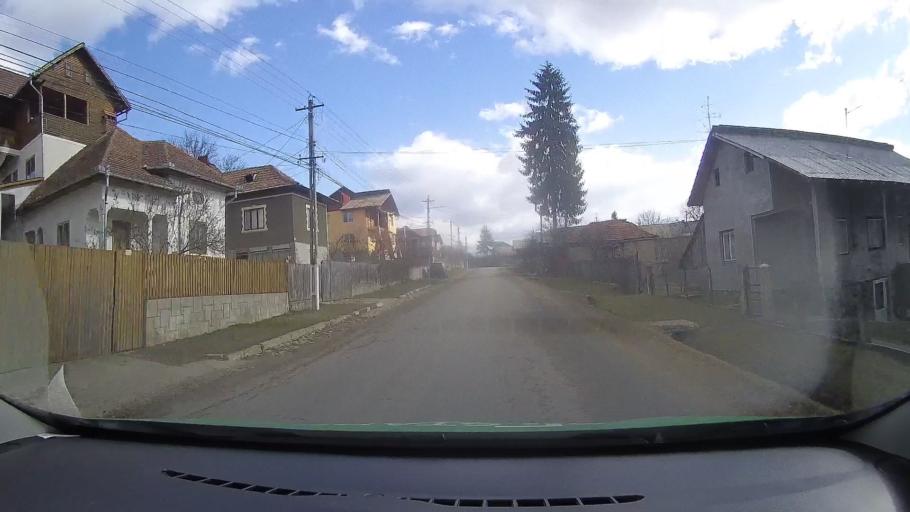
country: RO
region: Dambovita
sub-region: Comuna Buciumeni
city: Valea Leurzii
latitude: 45.1386
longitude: 25.4770
